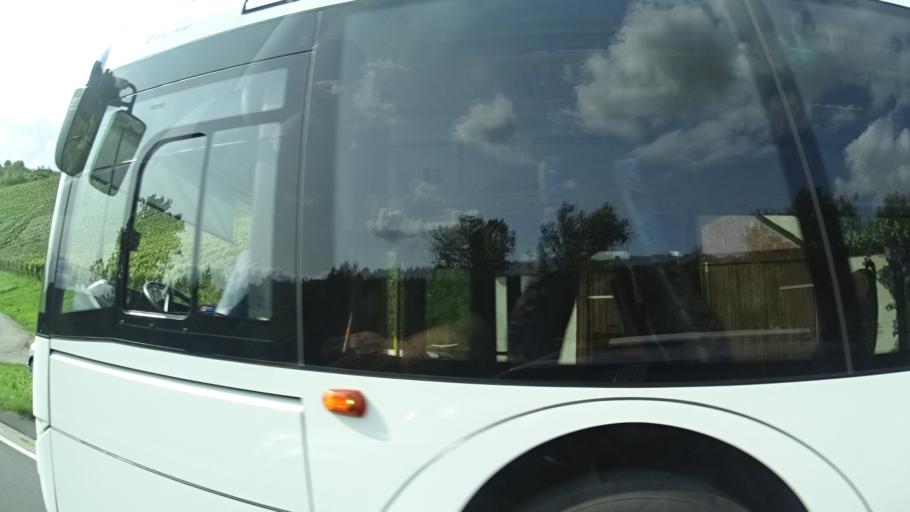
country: DE
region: Bavaria
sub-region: Regierungsbezirk Unterfranken
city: Retzstadt
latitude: 49.9113
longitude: 9.8605
